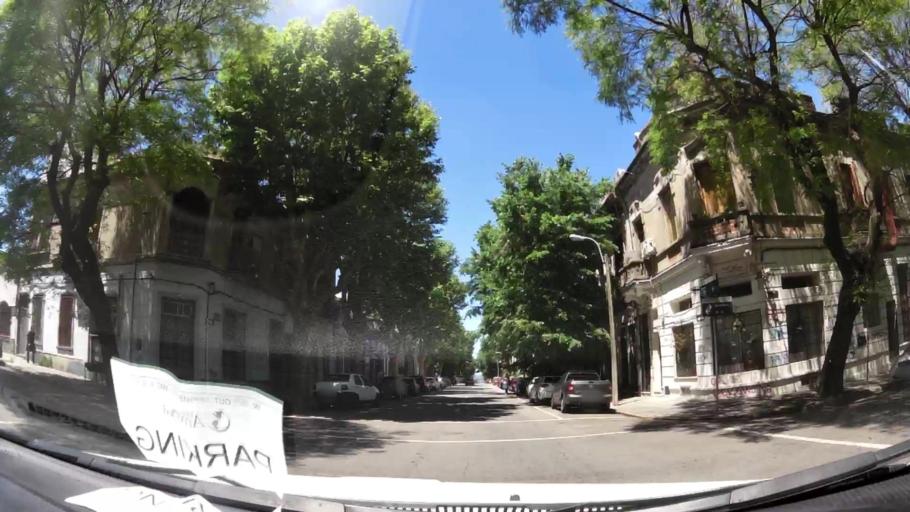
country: UY
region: Montevideo
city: Montevideo
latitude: -34.9103
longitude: -56.1740
